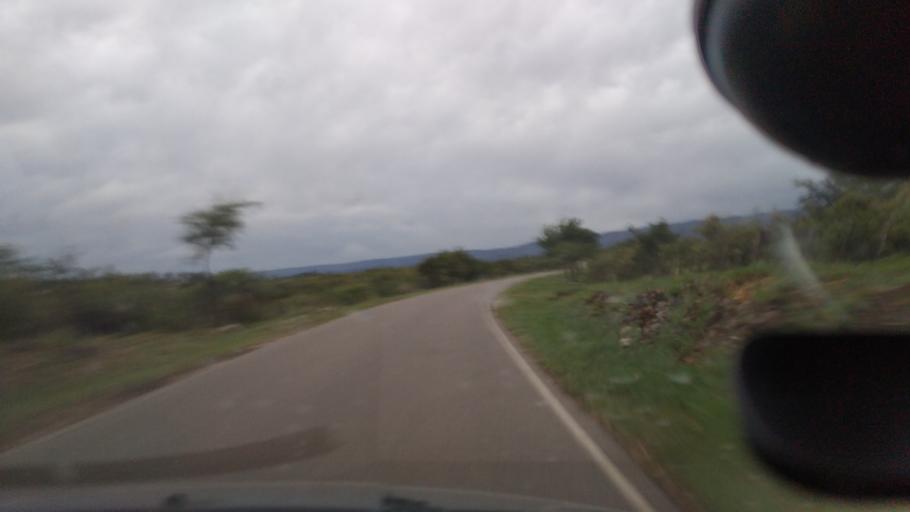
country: AR
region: Cordoba
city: Villa Las Rosas
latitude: -31.8889
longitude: -65.0306
